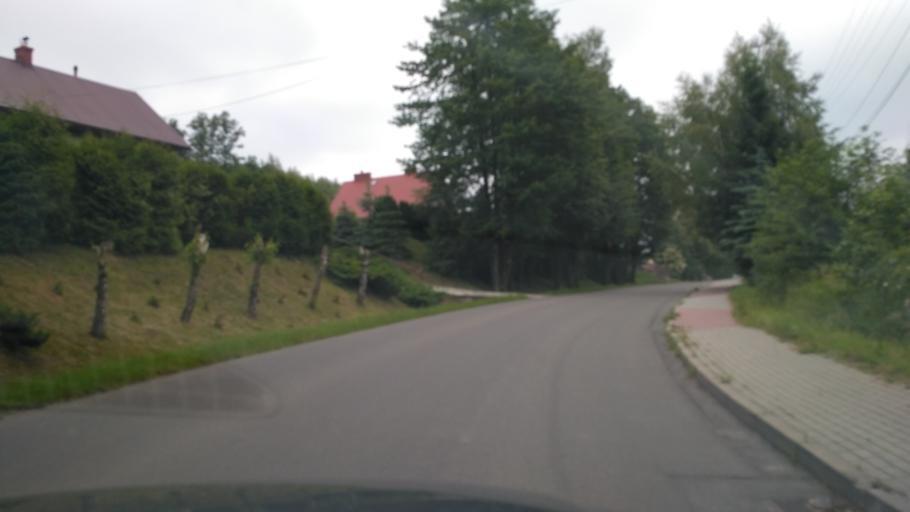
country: PL
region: Subcarpathian Voivodeship
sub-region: Powiat ropczycko-sedziszowski
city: Zagorzyce
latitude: 50.0317
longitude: 21.6866
